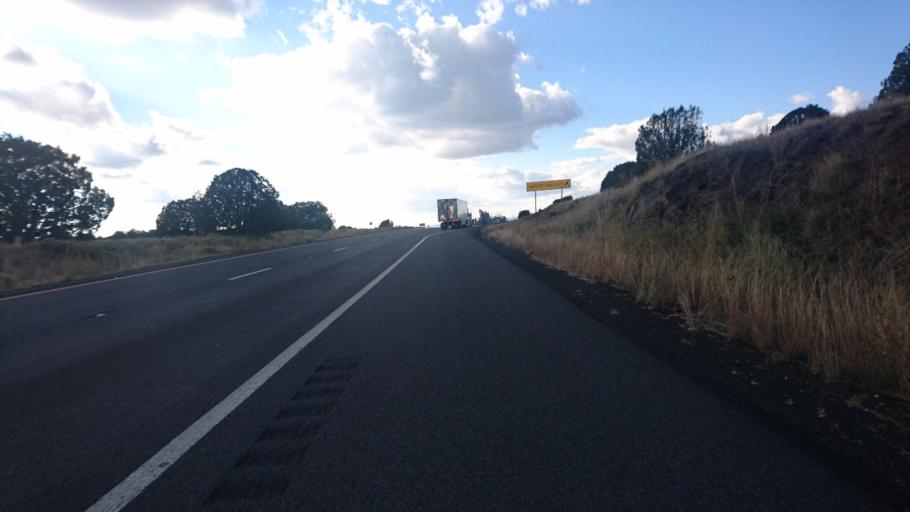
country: US
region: Arizona
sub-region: Coconino County
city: Williams
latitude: 35.2215
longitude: -112.3139
